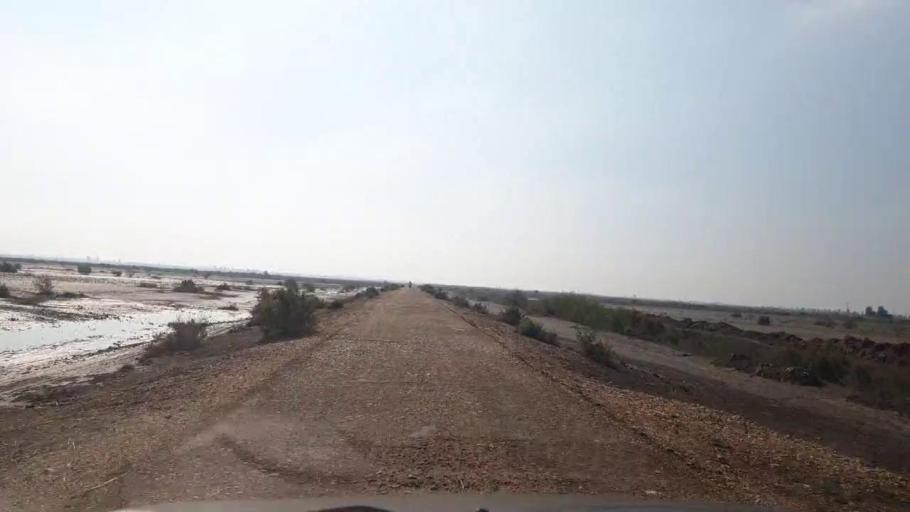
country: PK
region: Sindh
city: Sinjhoro
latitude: 26.0344
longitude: 68.7788
